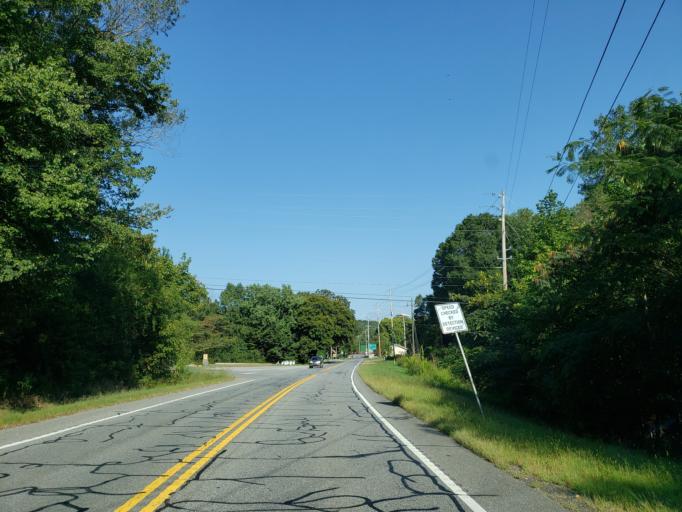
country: US
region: Georgia
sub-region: Whitfield County
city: Varnell
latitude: 34.9011
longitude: -84.9785
